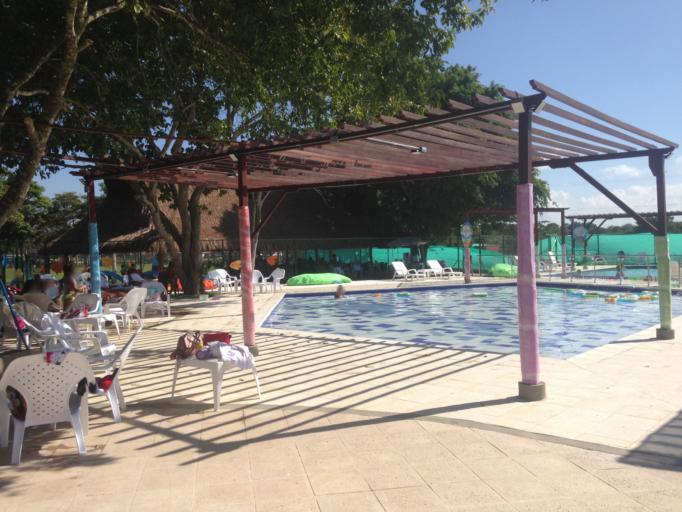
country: CO
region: Atlantico
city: Baranoa
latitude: 10.8415
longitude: -74.9031
